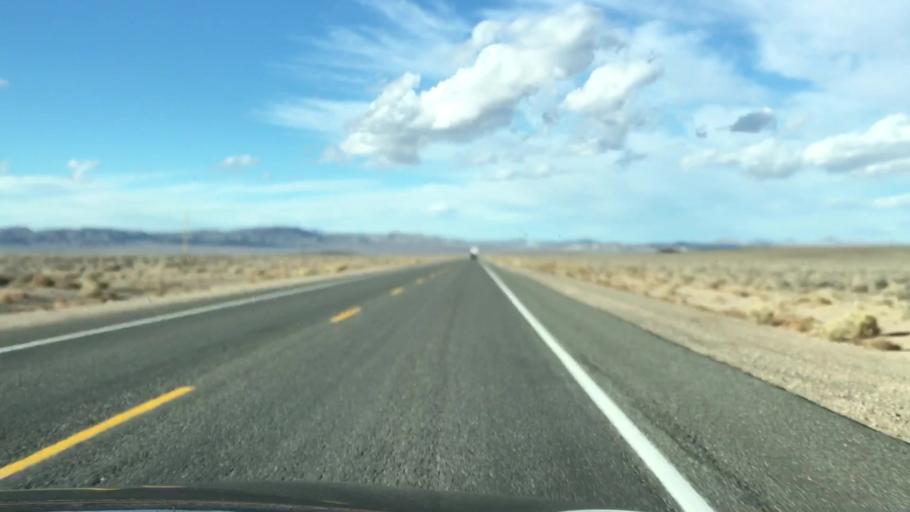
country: US
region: Nevada
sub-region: Esmeralda County
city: Goldfield
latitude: 37.4104
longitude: -117.1525
